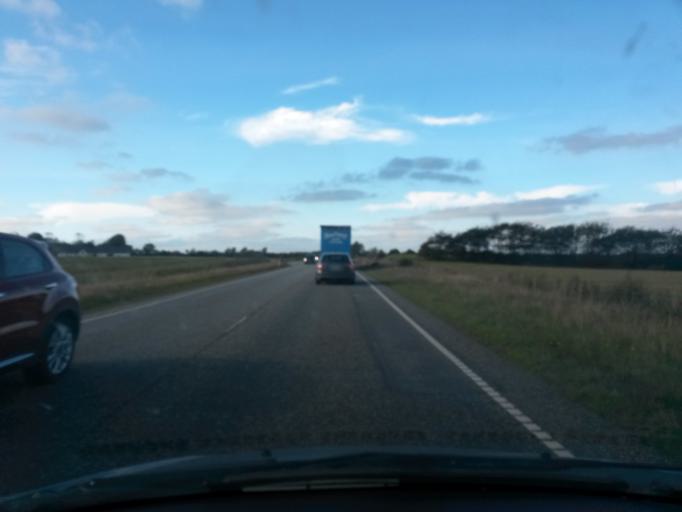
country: DK
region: Central Jutland
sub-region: Holstebro Kommune
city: Holstebro
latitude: 56.3168
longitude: 8.6842
